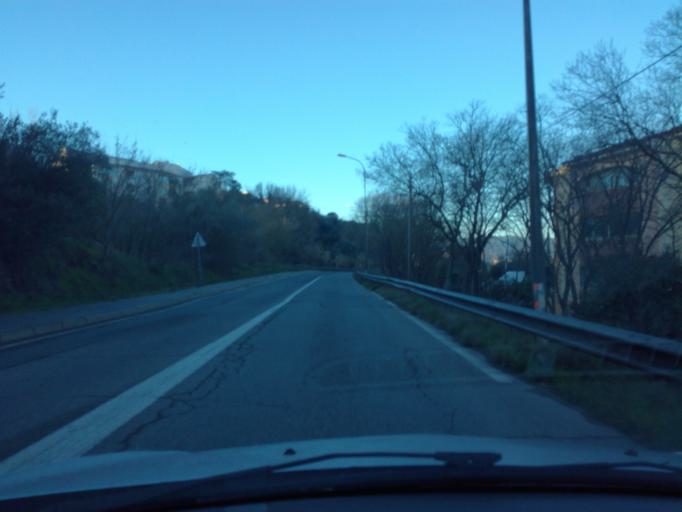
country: FR
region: Provence-Alpes-Cote d'Azur
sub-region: Departement du Var
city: Frejus
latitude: 43.4418
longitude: 6.7370
